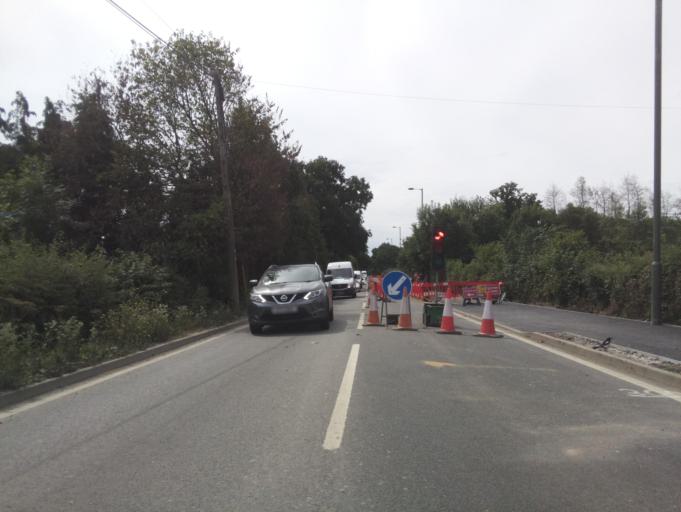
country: GB
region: England
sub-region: Surrey
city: Salfords
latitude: 51.1857
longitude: -0.1958
